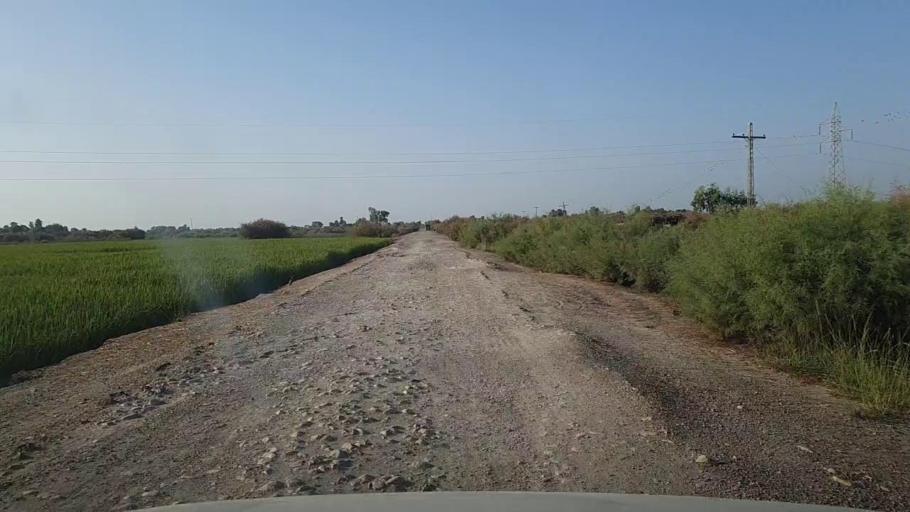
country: PK
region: Sindh
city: Kandhkot
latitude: 28.3077
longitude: 69.3283
